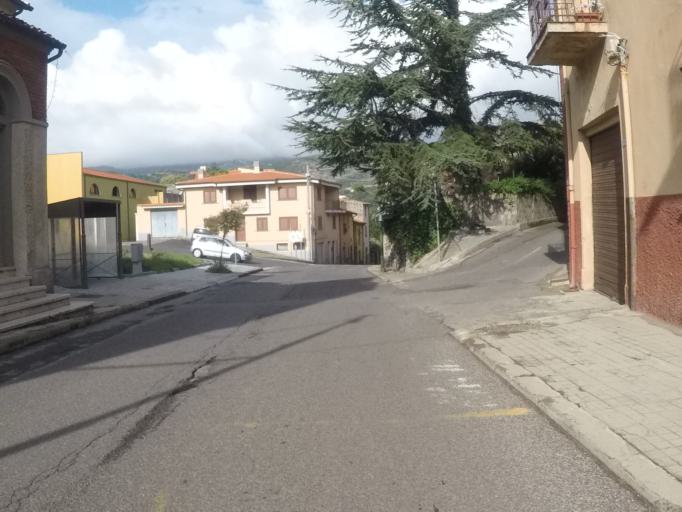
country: IT
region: Sardinia
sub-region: Provincia di Oristano
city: Santu Lussurgiu
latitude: 40.1417
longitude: 8.6585
